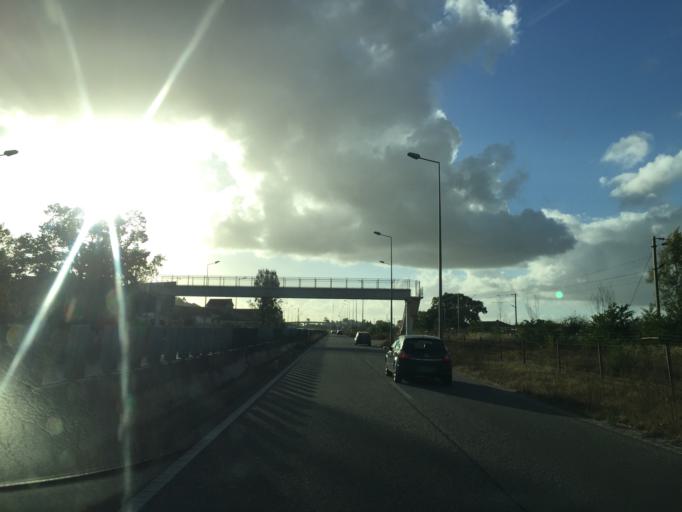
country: PT
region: Coimbra
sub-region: Coimbra
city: Coimbra
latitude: 40.2144
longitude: -8.4501
